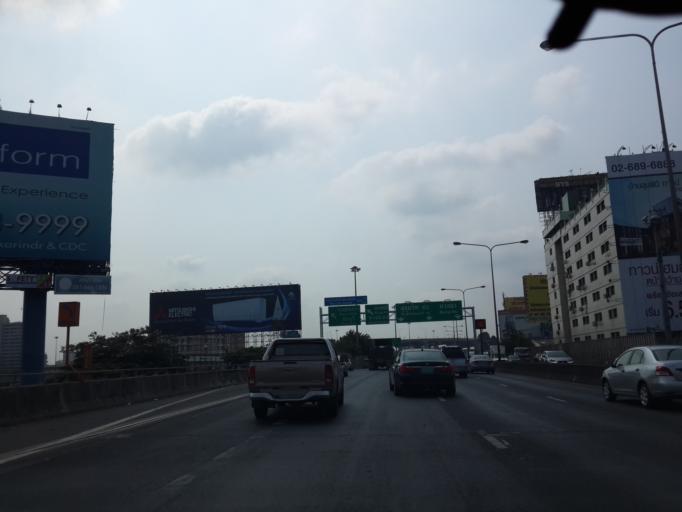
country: TH
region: Bangkok
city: Phra Khanong
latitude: 13.7051
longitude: 100.5890
